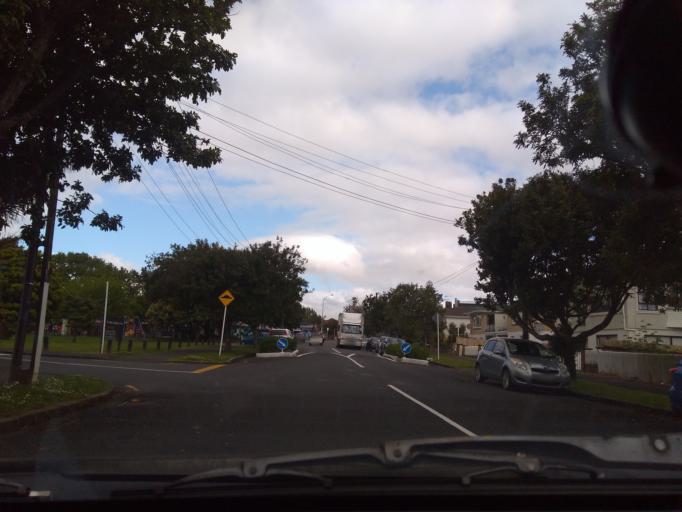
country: NZ
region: Auckland
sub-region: Auckland
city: Auckland
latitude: -36.8794
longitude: 174.7243
